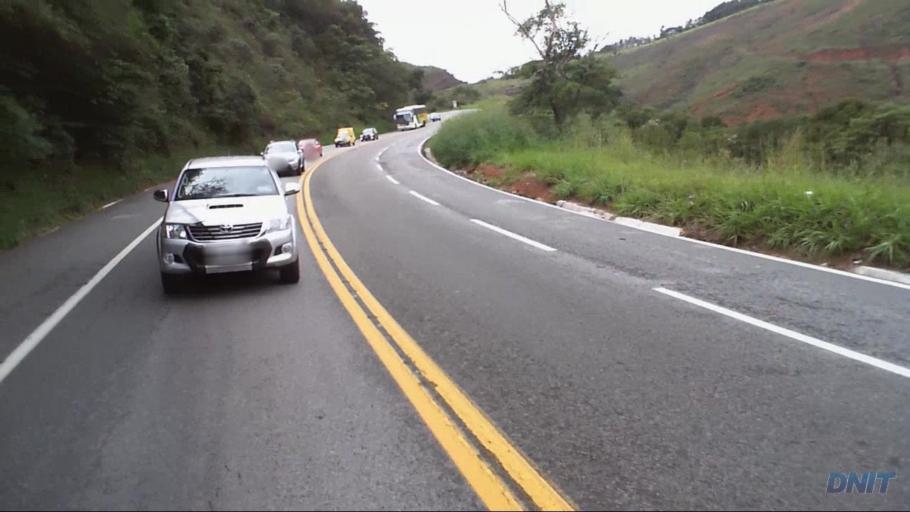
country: BR
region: Minas Gerais
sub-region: Joao Monlevade
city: Joao Monlevade
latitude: -19.8432
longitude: -43.3126
